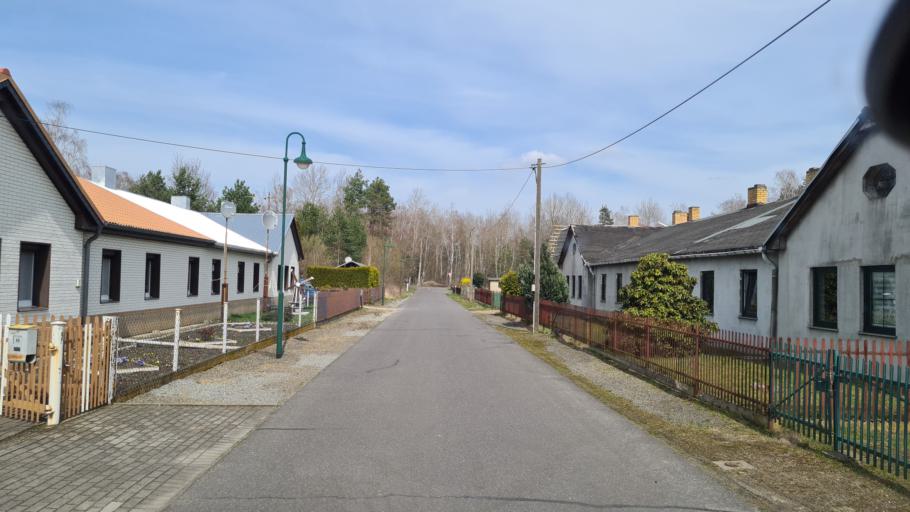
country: DE
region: Brandenburg
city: Lauchhammer
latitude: 51.5095
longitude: 13.7294
